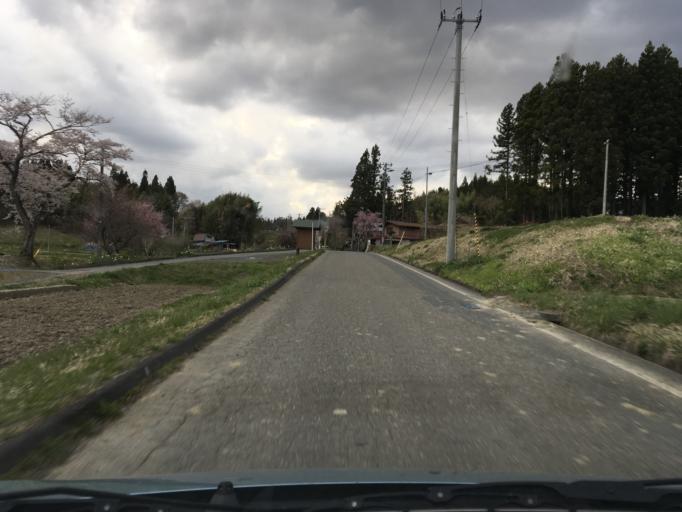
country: JP
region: Iwate
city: Ichinoseki
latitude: 38.9688
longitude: 141.2159
